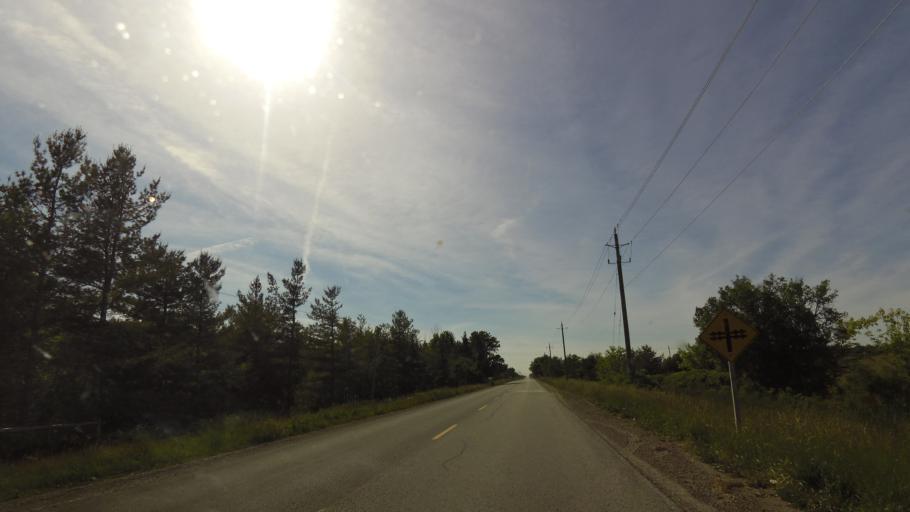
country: CA
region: Ontario
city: Ancaster
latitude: 43.0282
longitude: -80.0075
